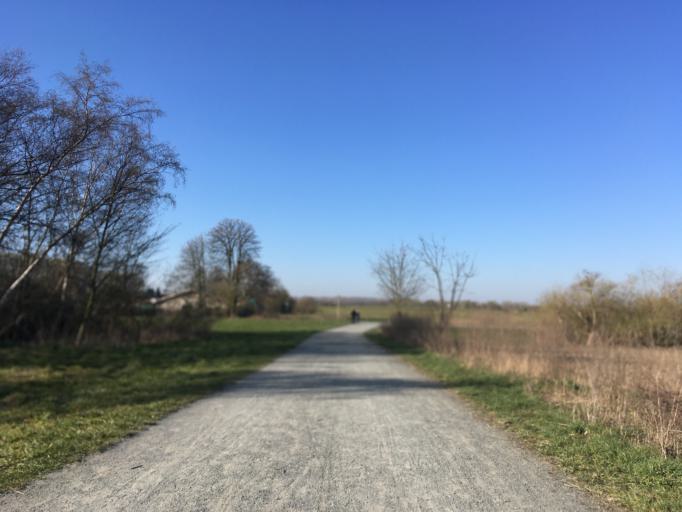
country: DE
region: Berlin
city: Blankenfelde
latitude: 52.6237
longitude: 13.4145
